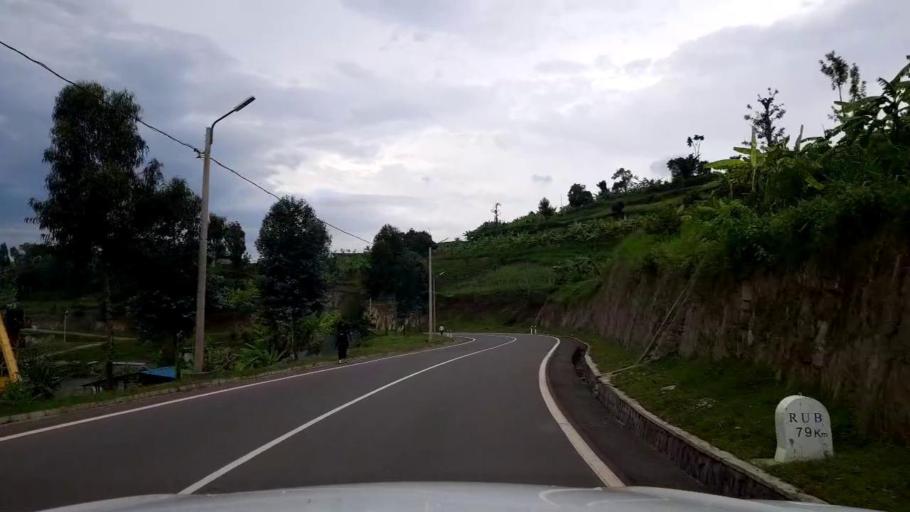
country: RW
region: Western Province
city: Kibuye
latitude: -2.0404
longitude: 29.4043
